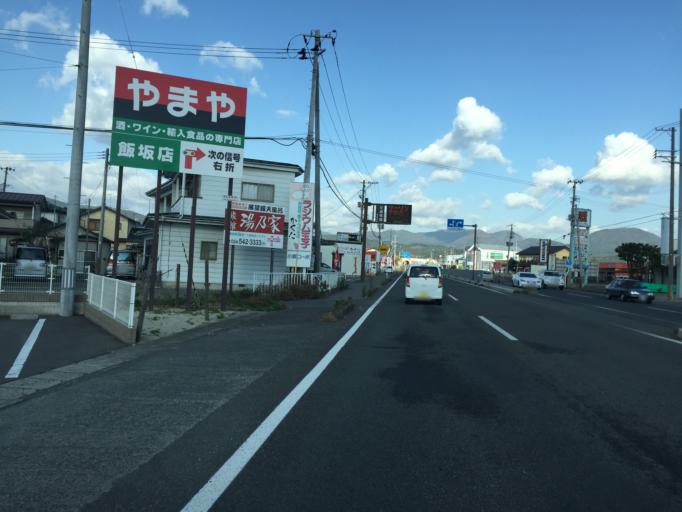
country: JP
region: Fukushima
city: Fukushima-shi
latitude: 37.8083
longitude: 140.4477
